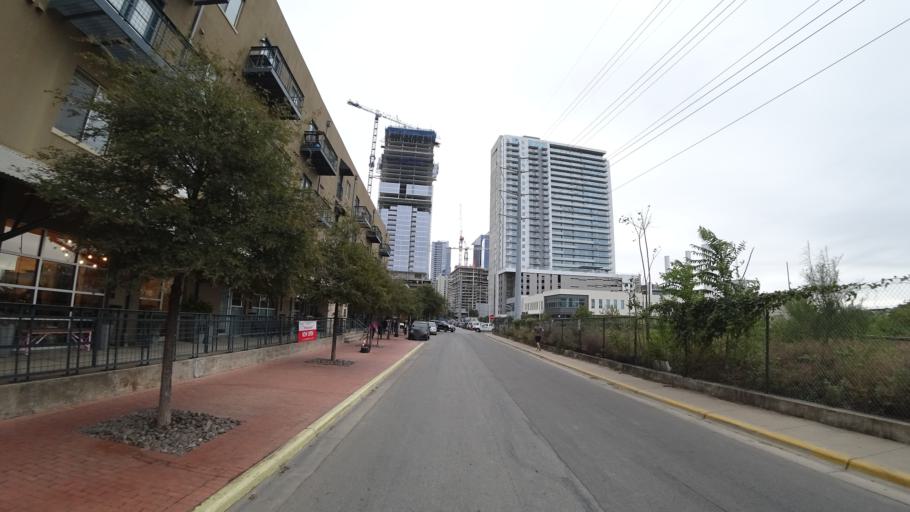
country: US
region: Texas
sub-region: Travis County
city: Austin
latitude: 30.2685
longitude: -97.7536
